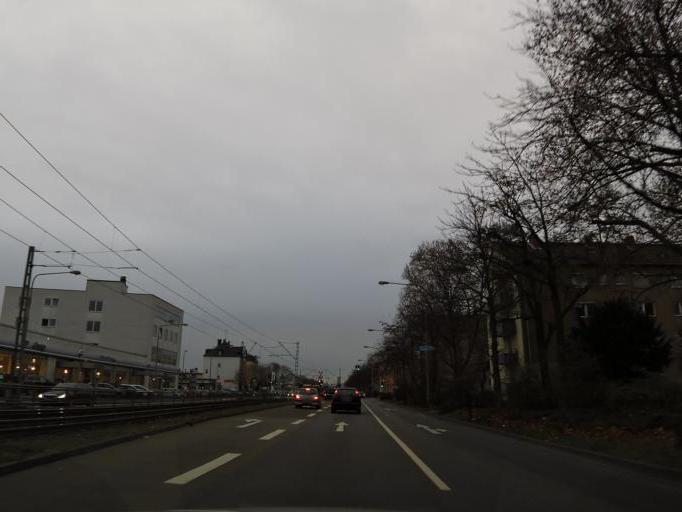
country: DE
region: Hesse
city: Niederrad
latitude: 50.1003
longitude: 8.5990
